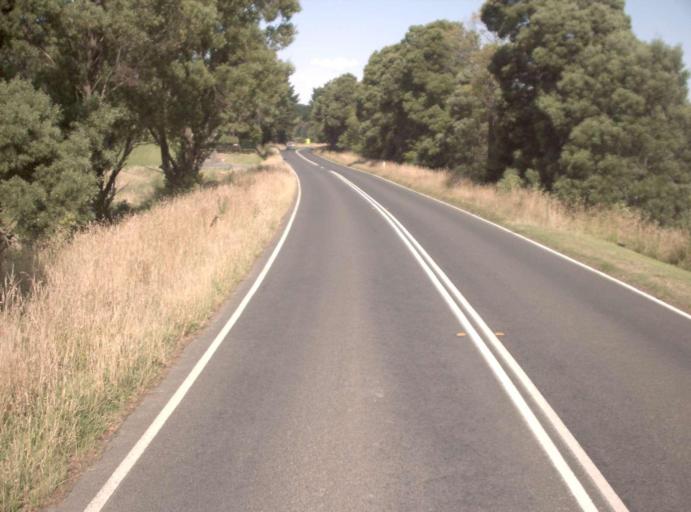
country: AU
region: Victoria
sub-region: Baw Baw
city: Warragul
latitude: -38.3563
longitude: 145.7888
